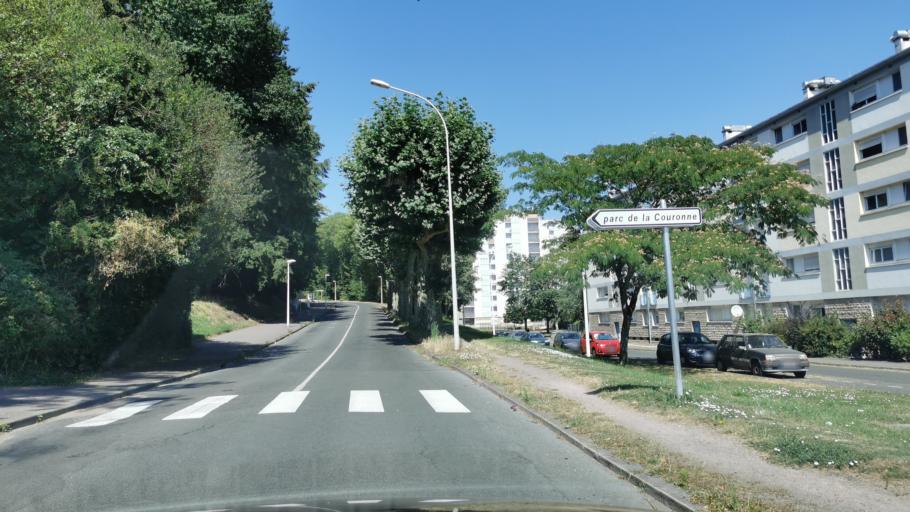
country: FR
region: Bourgogne
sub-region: Departement de Saone-et-Loire
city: Le Creusot
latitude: 46.8024
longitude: 4.4171
